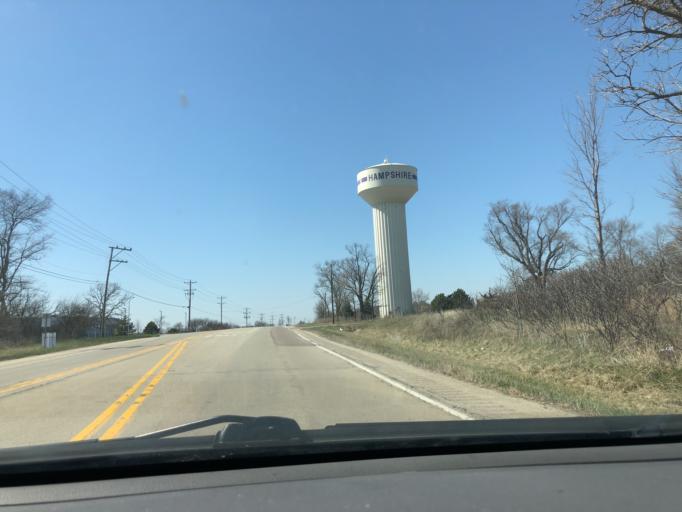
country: US
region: Illinois
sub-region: Kane County
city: Hampshire
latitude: 42.1351
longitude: -88.4993
